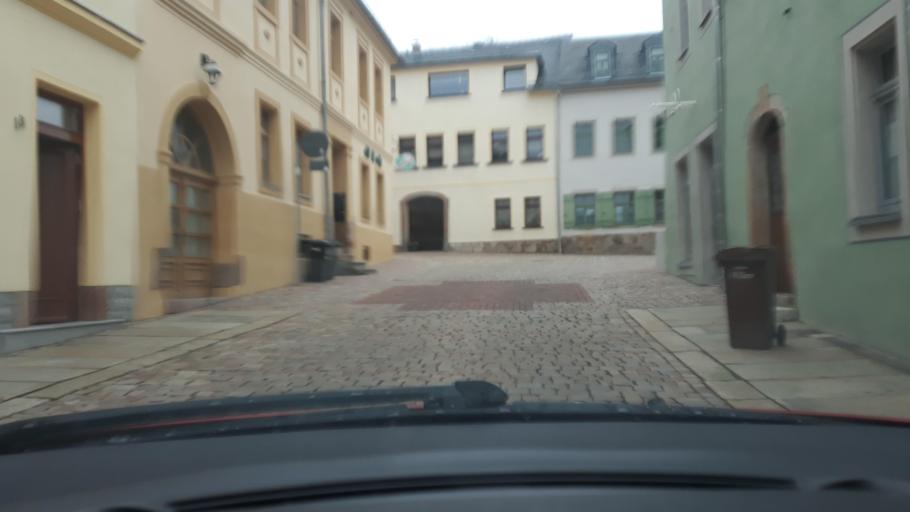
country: DE
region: Saxony
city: Kirchberg
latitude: 50.6206
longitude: 12.5273
